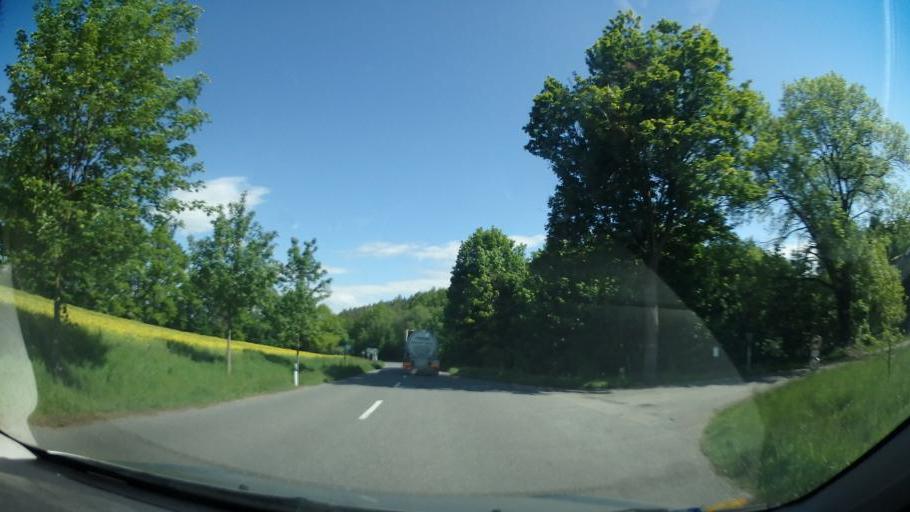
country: CZ
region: Pardubicky
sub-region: Okres Svitavy
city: Moravska Trebova
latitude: 49.6851
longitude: 16.6338
